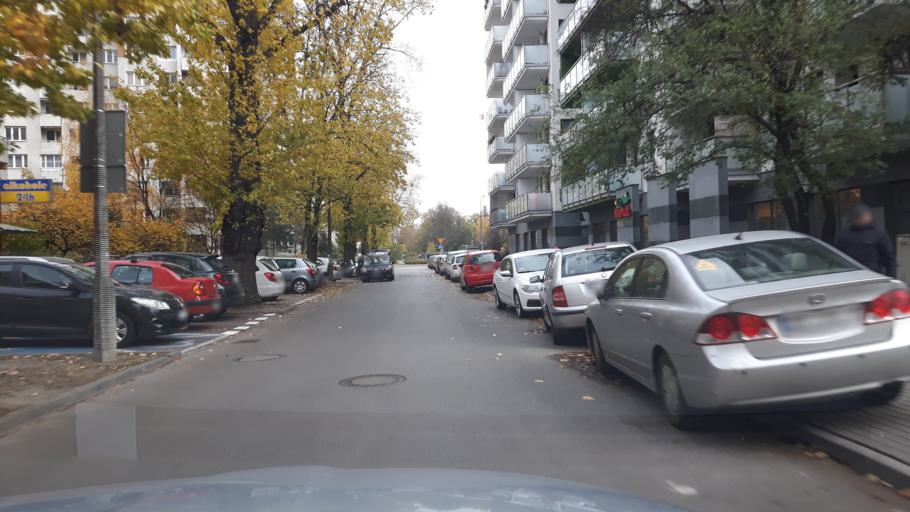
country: PL
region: Masovian Voivodeship
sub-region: Warszawa
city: Praga Polnoc
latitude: 52.2695
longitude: 21.0451
